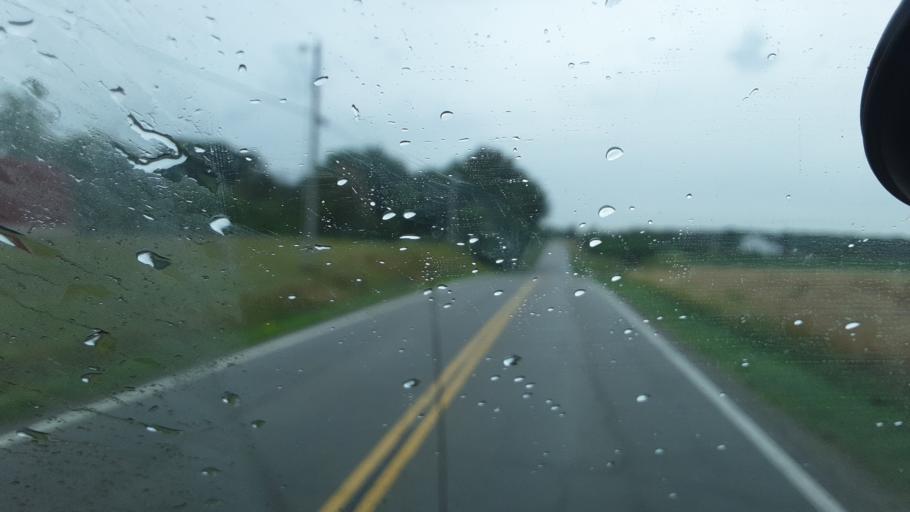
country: US
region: Ohio
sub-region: Williams County
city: Bryan
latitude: 41.5087
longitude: -84.6131
